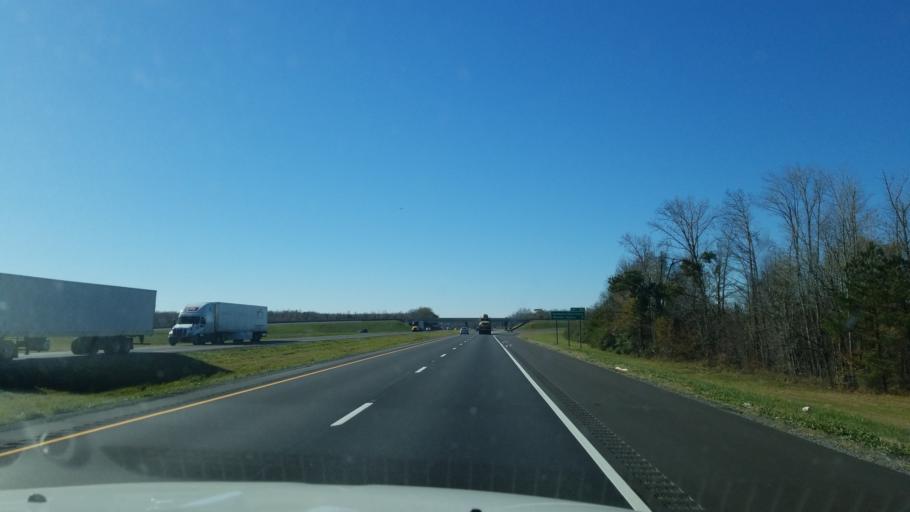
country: US
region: Alabama
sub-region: Tuscaloosa County
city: Tuscaloosa
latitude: 33.1544
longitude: -87.5932
